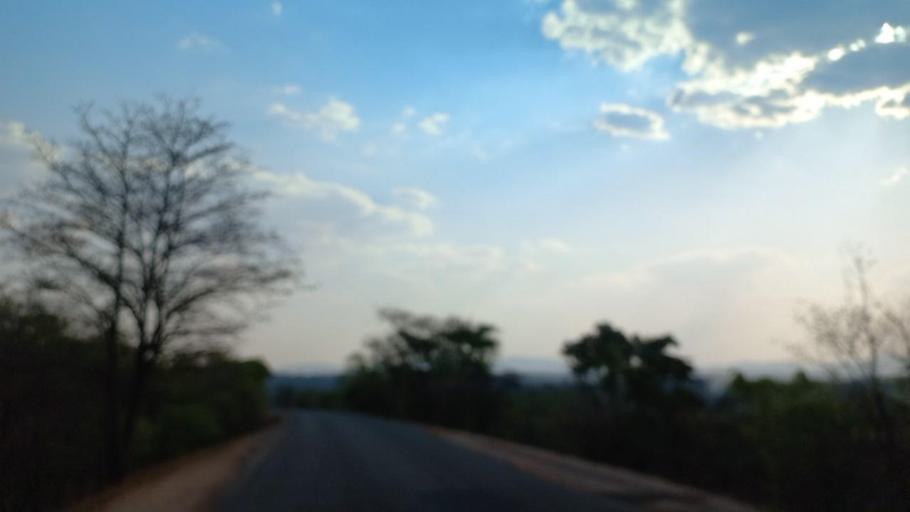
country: ZM
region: Lusaka
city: Luangwa
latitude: -15.0197
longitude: 29.9537
